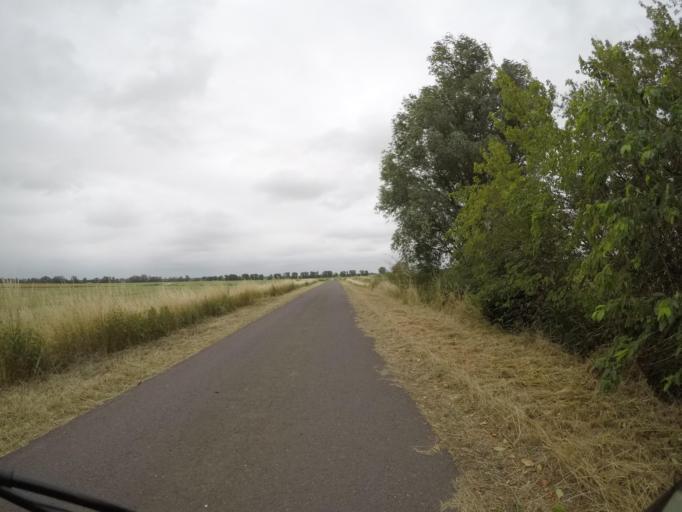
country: DE
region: Lower Saxony
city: Hitzacker
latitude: 53.1722
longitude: 11.0900
